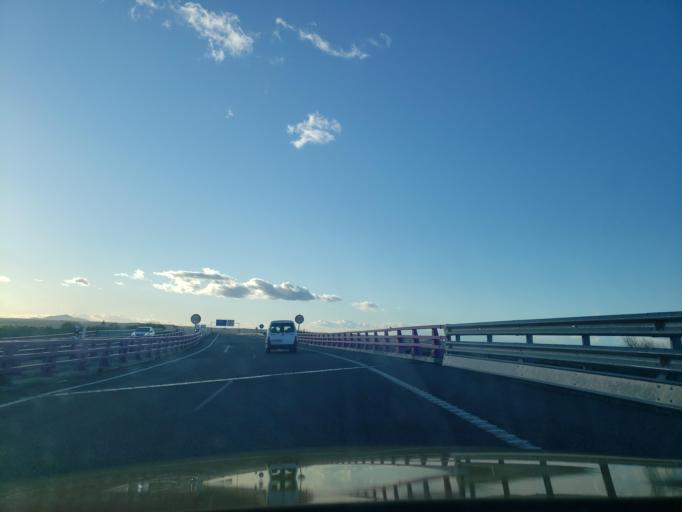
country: ES
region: Castille-La Mancha
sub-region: Province of Toledo
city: Burguillos de Toledo
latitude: 39.8169
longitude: -3.9797
